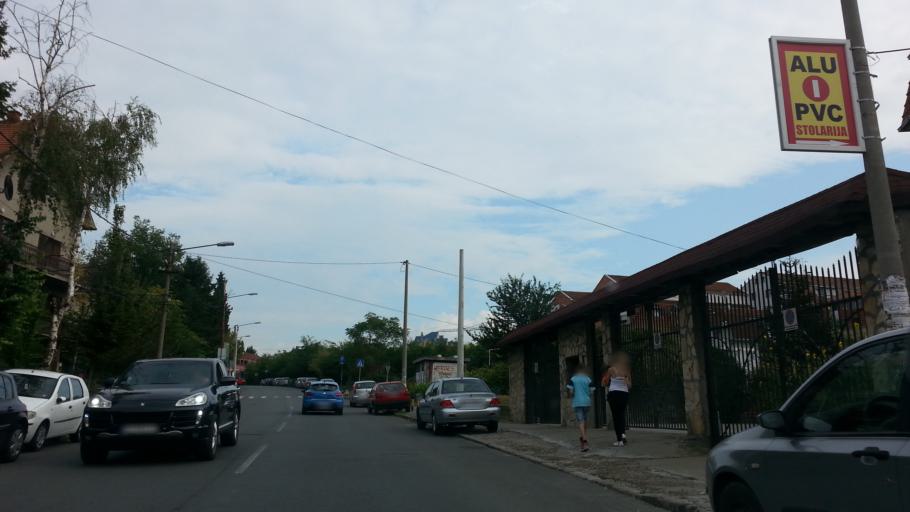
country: RS
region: Central Serbia
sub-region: Belgrade
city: Rakovica
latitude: 44.7548
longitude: 20.4226
